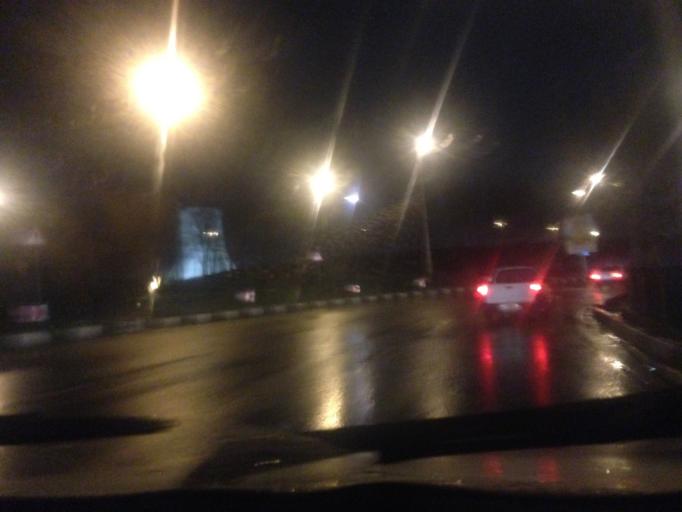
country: IR
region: Tehran
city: Tehran
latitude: 35.6969
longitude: 51.3389
